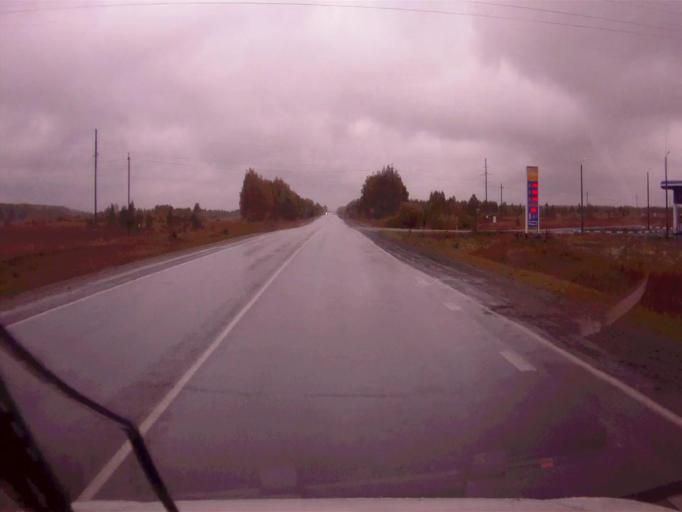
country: RU
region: Chelyabinsk
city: Argayash
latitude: 55.4777
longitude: 60.8525
